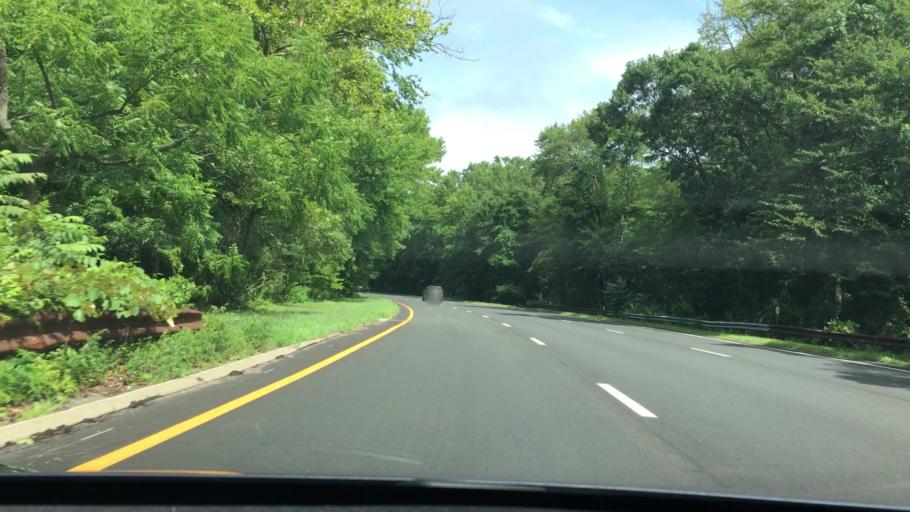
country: US
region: New York
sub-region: Nassau County
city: Wantagh
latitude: 40.6771
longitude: -73.5126
